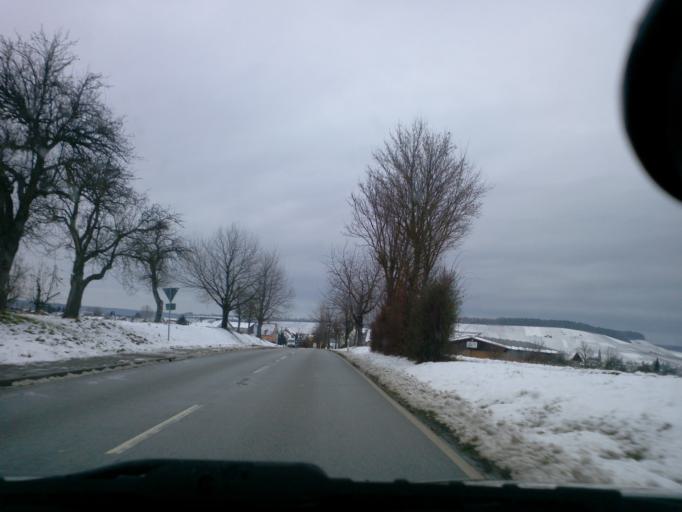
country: DE
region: Baden-Wuerttemberg
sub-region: Regierungsbezirk Stuttgart
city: Brackenheim
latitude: 49.0821
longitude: 9.0816
